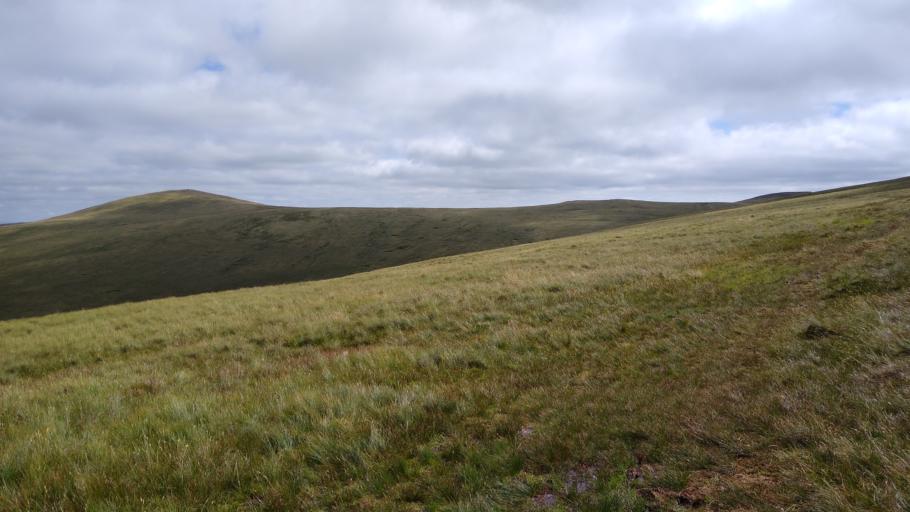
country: GB
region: England
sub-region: Cumbria
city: Keswick
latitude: 54.6532
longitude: -3.0586
